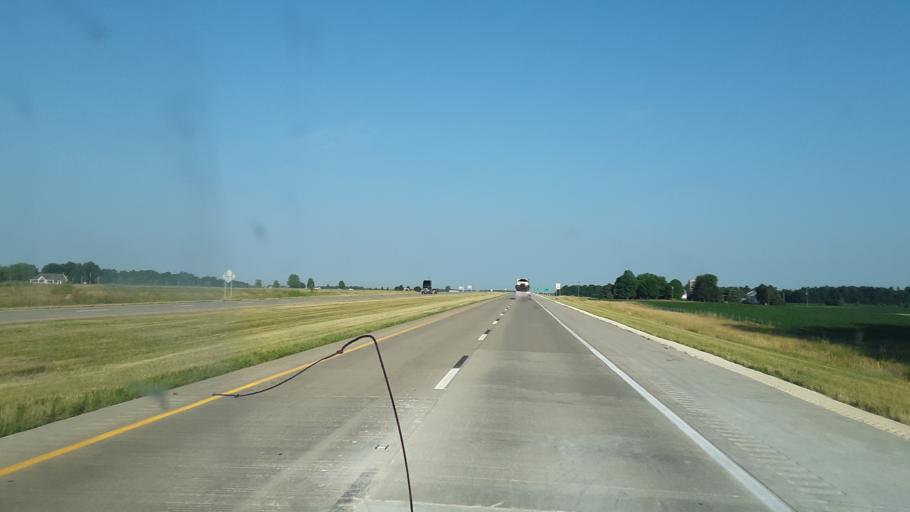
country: US
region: Ohio
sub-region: Wyandot County
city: Upper Sandusky
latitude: 40.8083
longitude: -83.1928
